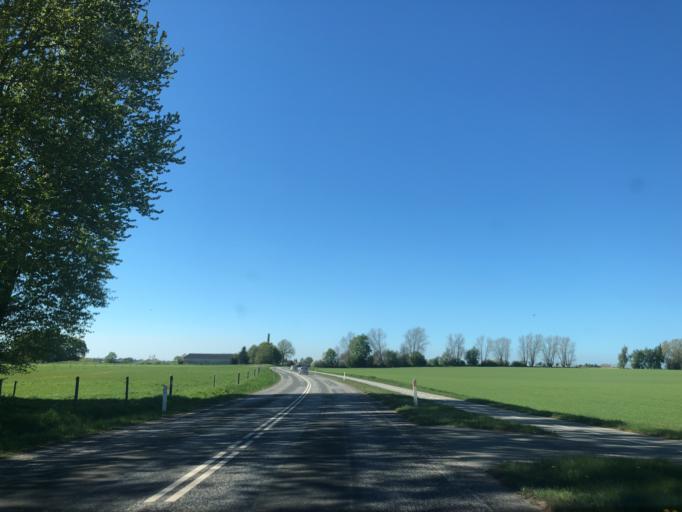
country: DK
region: Zealand
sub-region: Stevns Kommune
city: Stroby Egede
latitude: 55.3723
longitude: 12.2985
